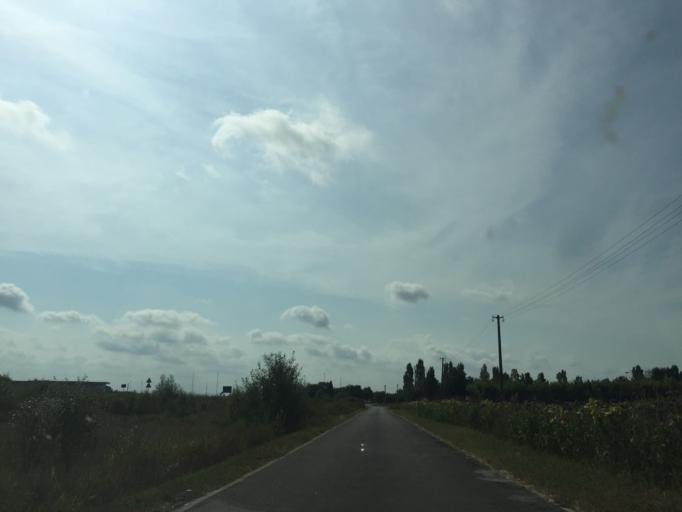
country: IT
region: Tuscany
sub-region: Provincia di Pistoia
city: Cintolese
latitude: 43.8407
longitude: 10.8191
